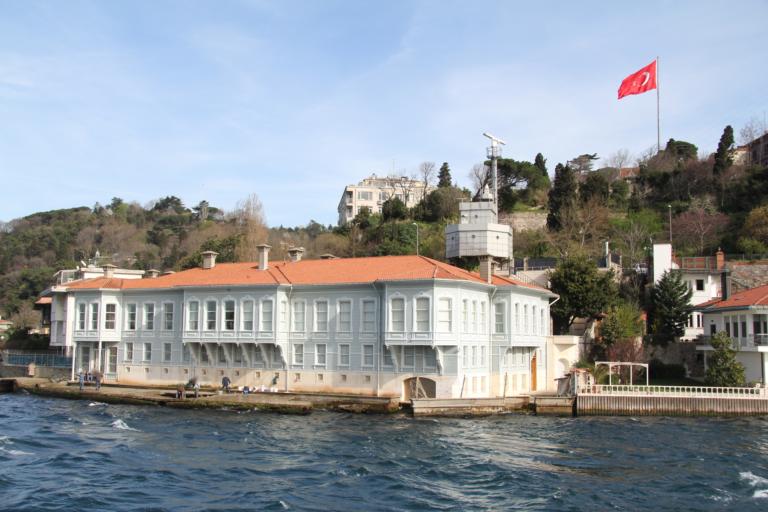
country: TR
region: Istanbul
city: UEskuedar
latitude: 41.0739
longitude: 29.0547
